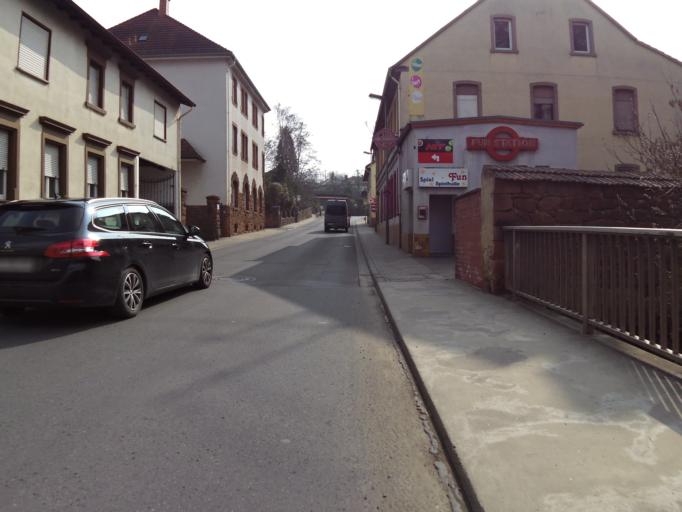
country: DE
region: Rheinland-Pfalz
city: Eisenberg
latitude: 49.5562
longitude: 8.0715
